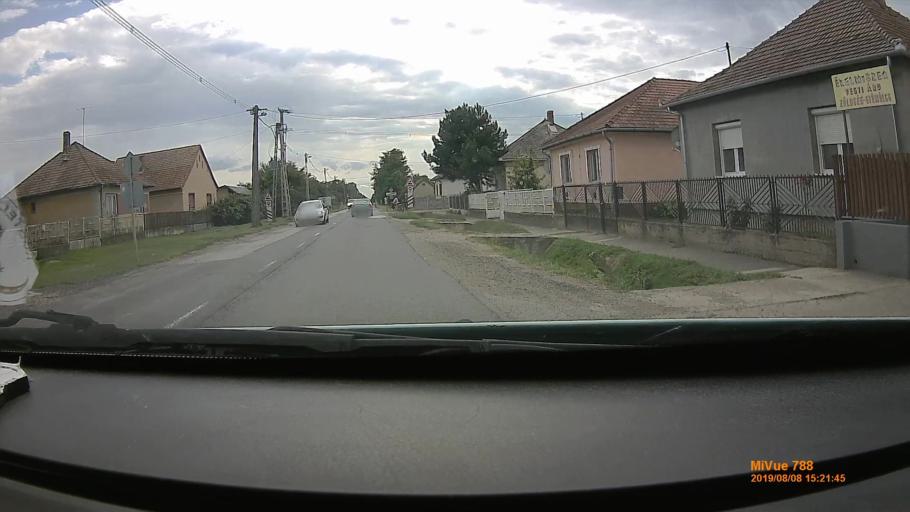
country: HU
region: Szabolcs-Szatmar-Bereg
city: Tunyogmatolcs
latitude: 47.9640
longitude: 22.4465
